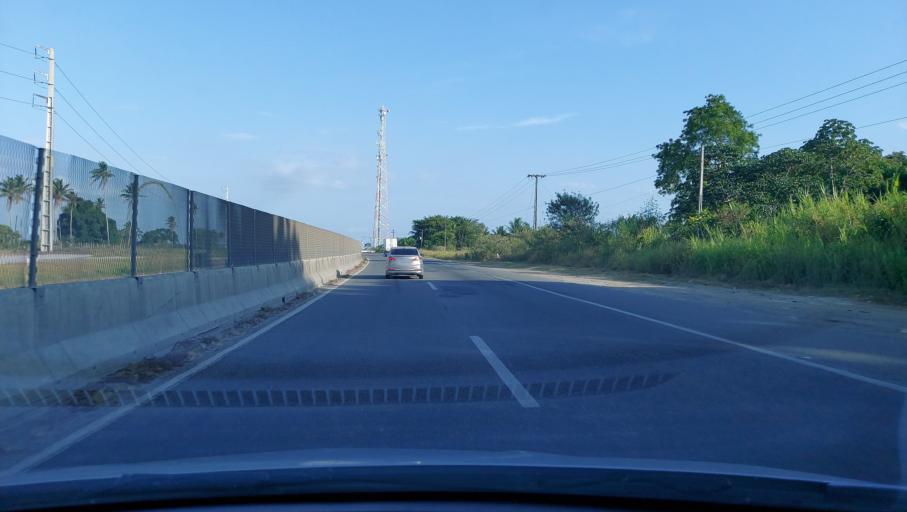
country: BR
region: Bahia
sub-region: Conceicao Do Jacuipe
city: Conceicao do Jacuipe
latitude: -12.3888
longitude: -38.7880
